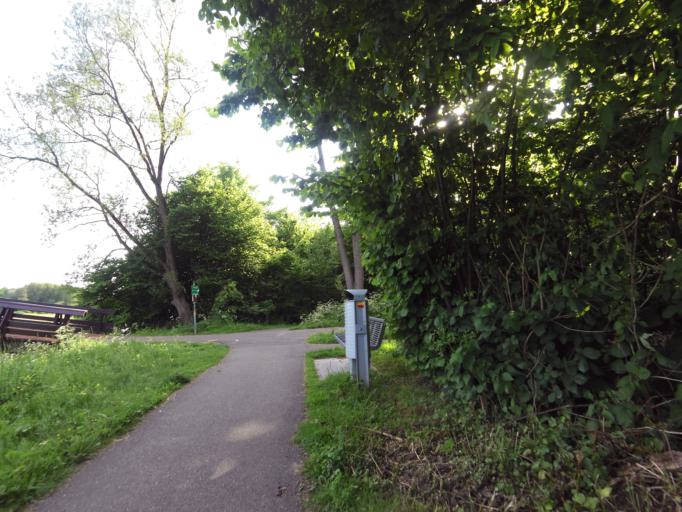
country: NL
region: South Holland
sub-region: Gemeente Zoetermeer
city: Zoetermeer
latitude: 52.0597
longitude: 4.4532
